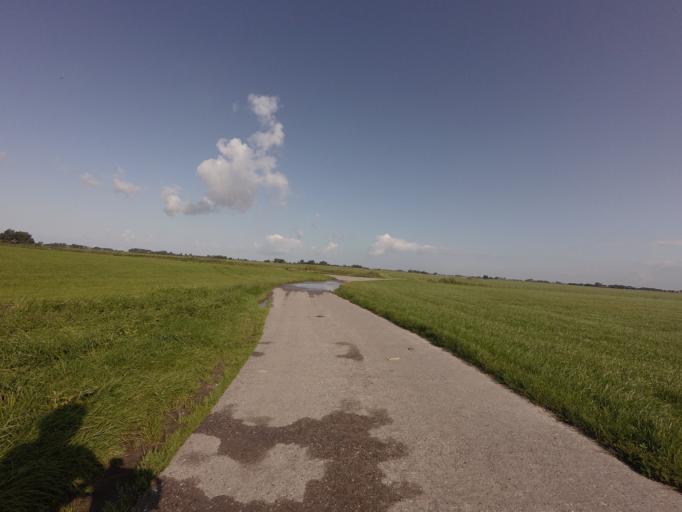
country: NL
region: Friesland
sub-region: Gemeente Franekeradeel
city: Franeker
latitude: 53.2032
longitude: 5.5766
